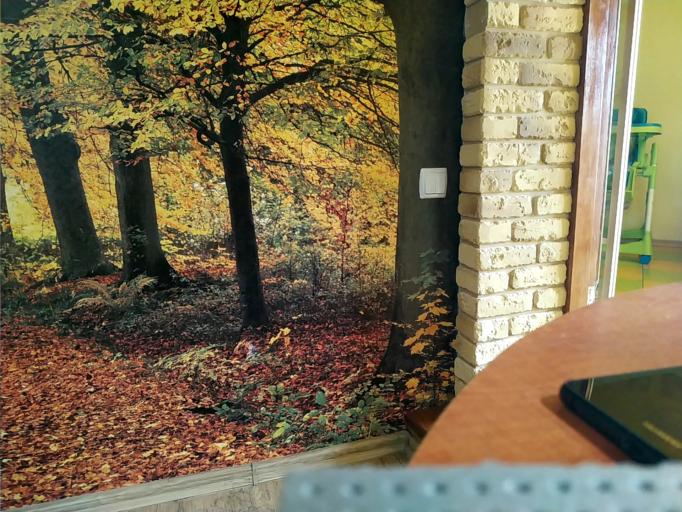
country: RU
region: Tverskaya
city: Kalashnikovo
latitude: 57.2817
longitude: 35.1159
